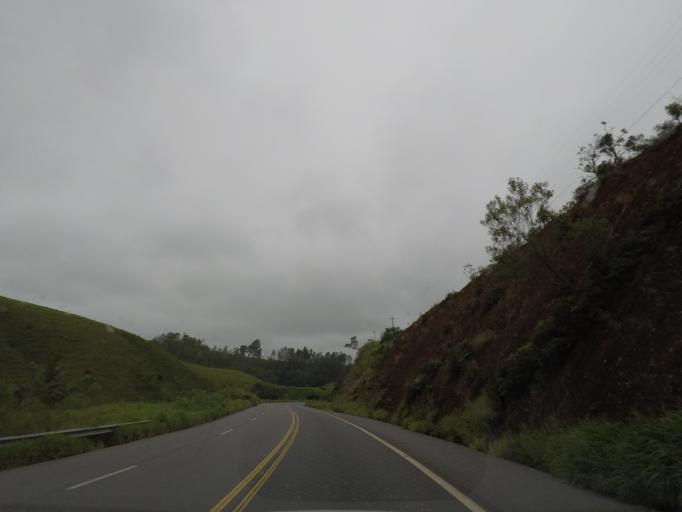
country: BR
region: Sao Paulo
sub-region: Cunha
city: Cunha
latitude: -22.9382
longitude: -45.0678
